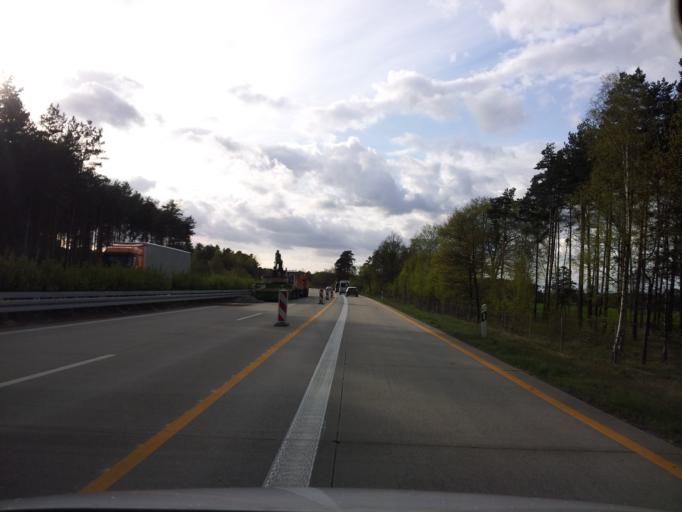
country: DE
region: Brandenburg
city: Cottbus
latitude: 51.7133
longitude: 14.3949
